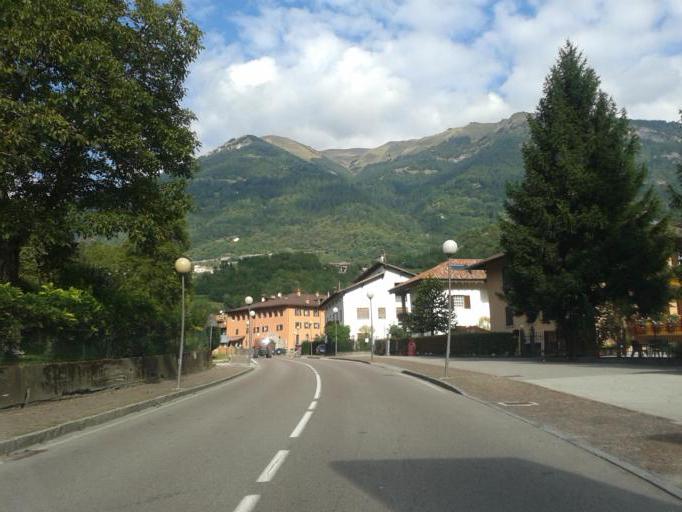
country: IT
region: Trentino-Alto Adige
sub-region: Provincia di Trento
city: Creto
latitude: 45.9362
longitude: 10.6389
